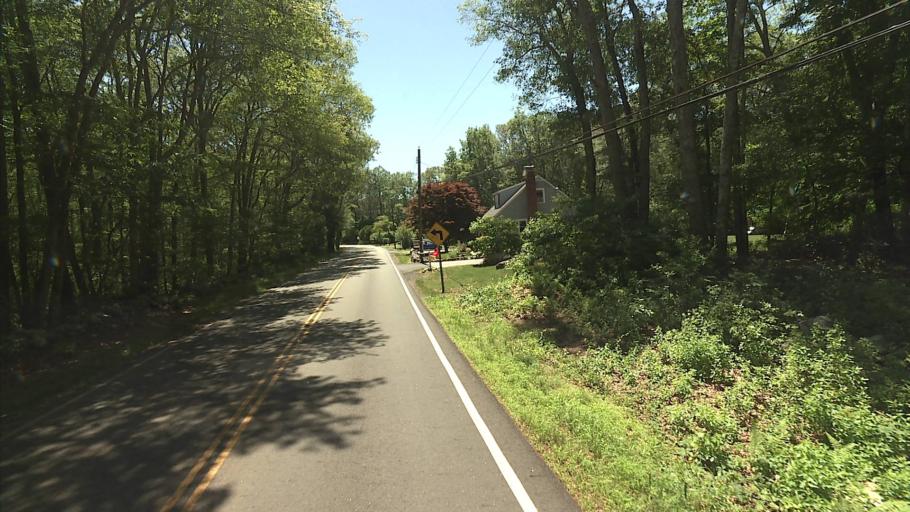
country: US
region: Connecticut
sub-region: New London County
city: Old Mystic
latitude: 41.3776
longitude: -71.9220
